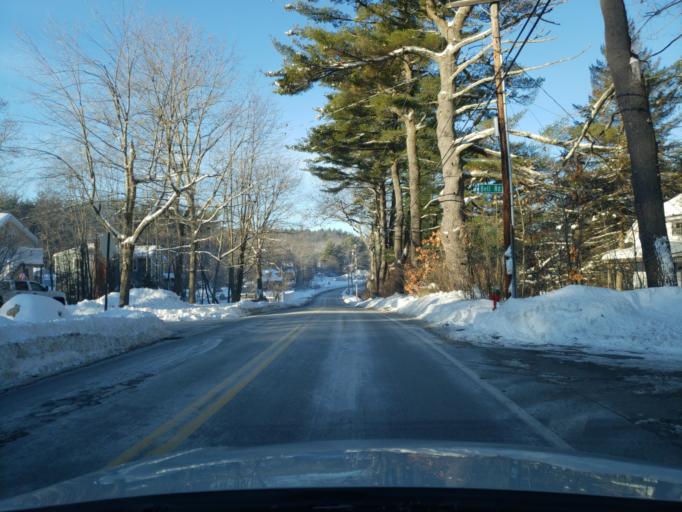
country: US
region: New Hampshire
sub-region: Hillsborough County
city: Goffstown
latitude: 43.0156
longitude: -71.6084
